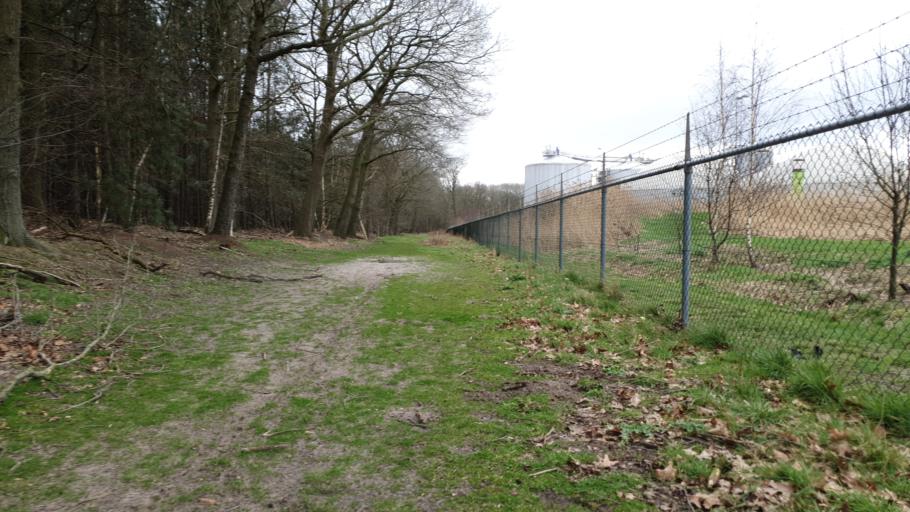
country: NL
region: North Brabant
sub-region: Gemeente Son en Breugel
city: Son
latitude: 51.5081
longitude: 5.4467
